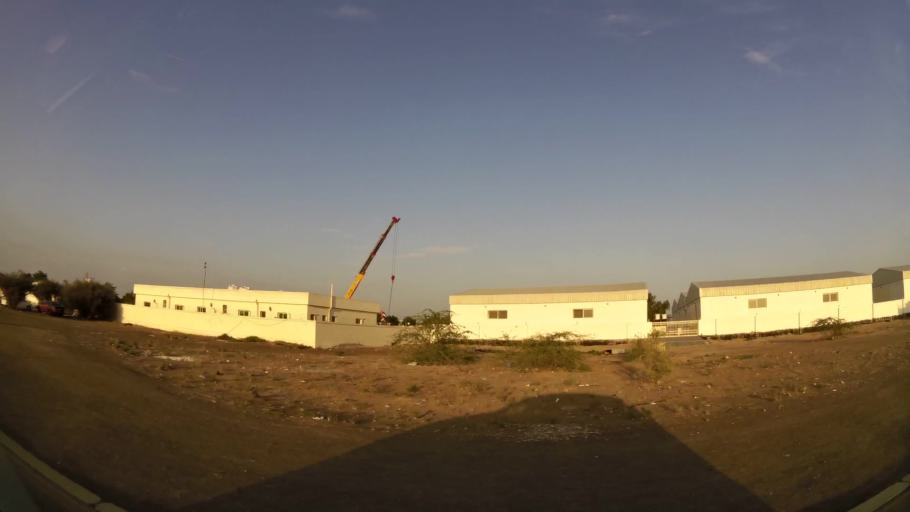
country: AE
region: Abu Dhabi
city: Al Ain
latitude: 24.1548
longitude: 55.8113
